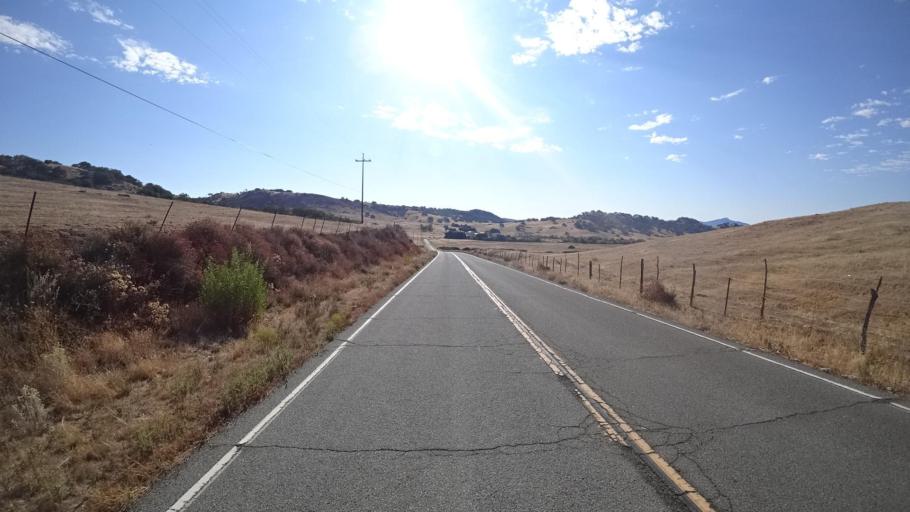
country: US
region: California
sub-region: San Diego County
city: Julian
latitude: 33.1640
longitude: -116.7338
